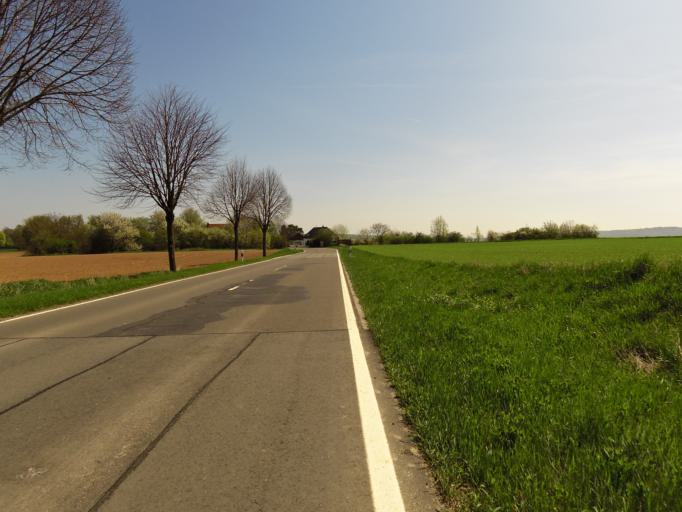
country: DE
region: Rheinland-Pfalz
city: Lautersheim
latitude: 49.5870
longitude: 8.0909
